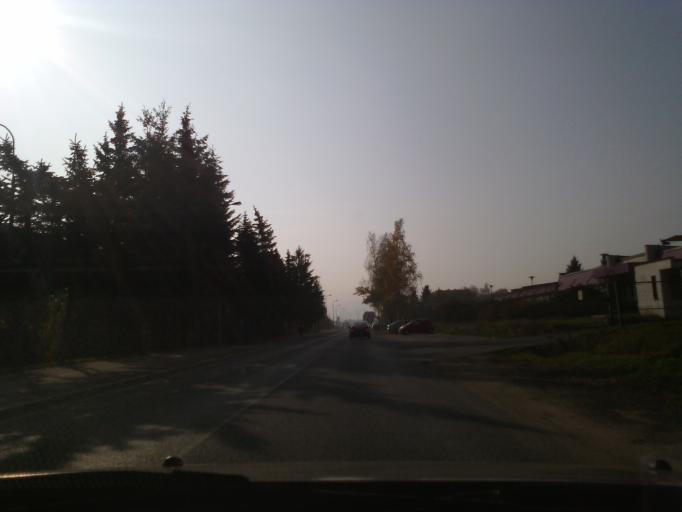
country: PL
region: Lower Silesian Voivodeship
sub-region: Jelenia Gora
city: Jelenia Gora
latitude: 50.8896
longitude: 15.7041
